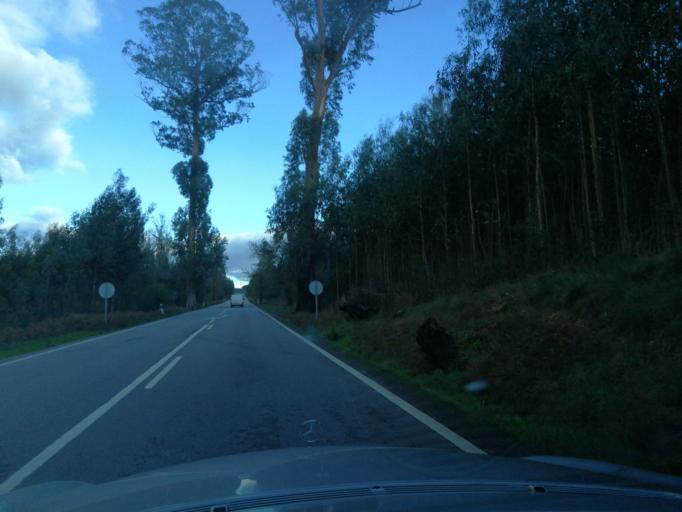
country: PT
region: Braga
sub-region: Barcelos
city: Vila Frescainha
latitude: 41.5727
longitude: -8.7076
